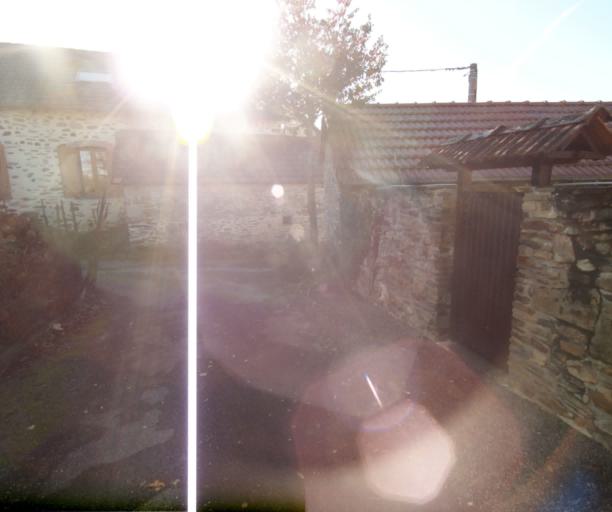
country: FR
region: Limousin
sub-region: Departement de la Correze
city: Laguenne
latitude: 45.2391
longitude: 1.7510
